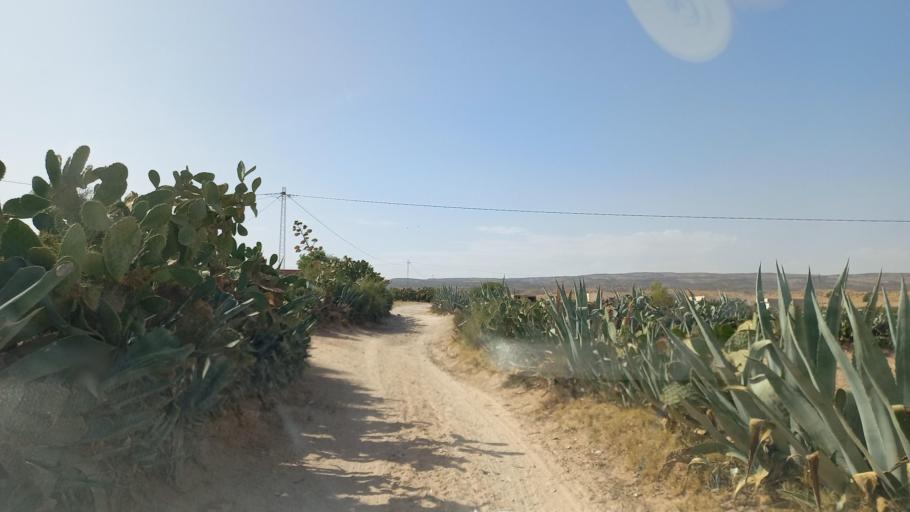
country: TN
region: Al Qasrayn
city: Kasserine
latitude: 35.2769
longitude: 8.9424
